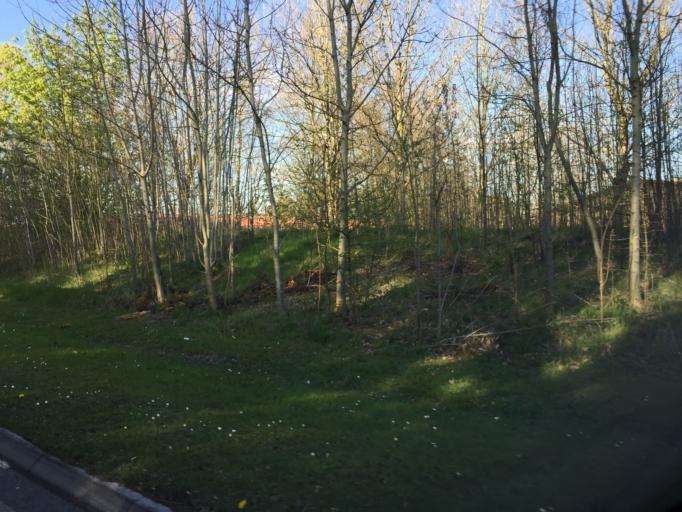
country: GB
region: Wales
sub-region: Torfaen County Borough
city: Cwmbran
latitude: 51.6352
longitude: -3.0203
